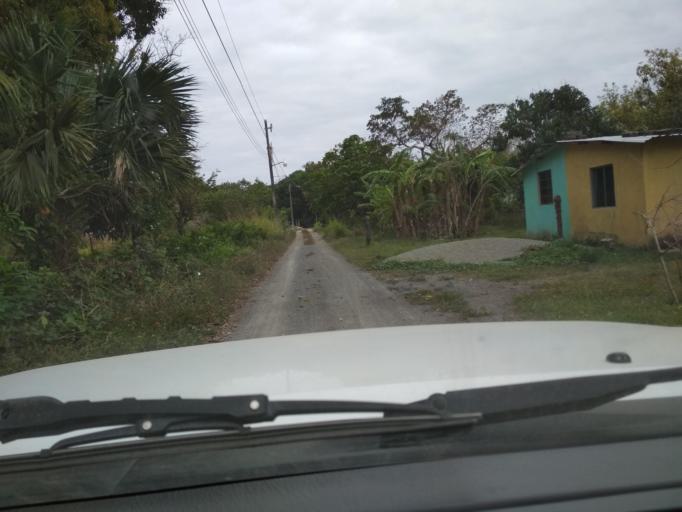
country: MX
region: Veracruz
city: El Tejar
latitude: 19.0730
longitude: -96.1352
